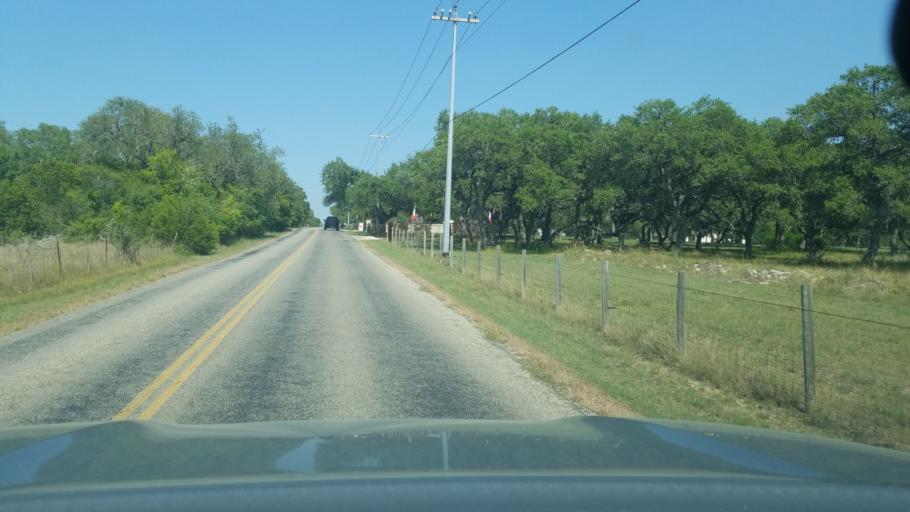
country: US
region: Texas
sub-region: Bexar County
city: Fair Oaks Ranch
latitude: 29.7855
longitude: -98.6423
